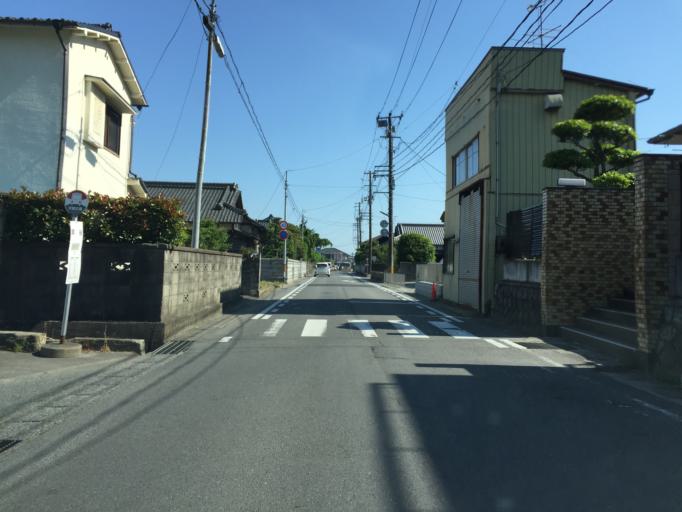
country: JP
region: Fukushima
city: Iwaki
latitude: 36.9984
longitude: 140.8541
